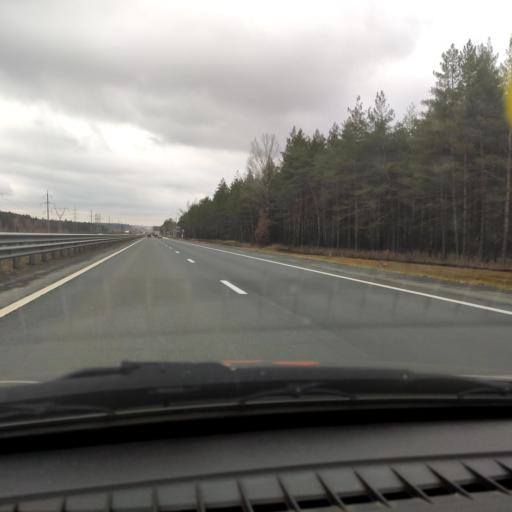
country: RU
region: Samara
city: Povolzhskiy
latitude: 53.5158
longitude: 49.7023
